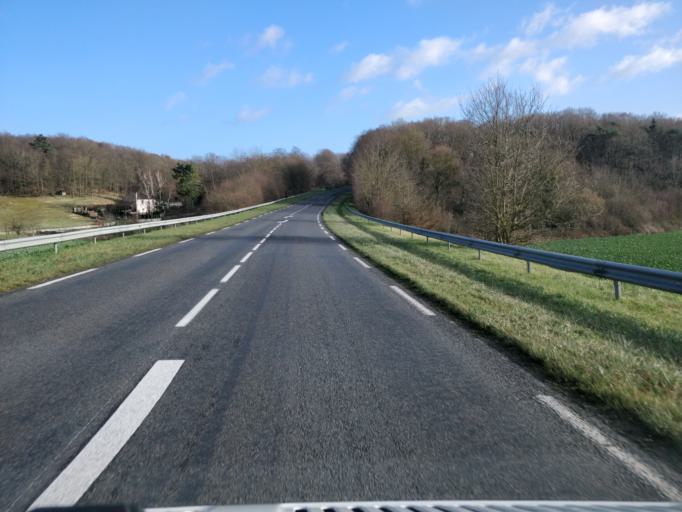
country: FR
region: Ile-de-France
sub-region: Departement de Seine-et-Marne
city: Lorrez-le-Bocage-Preaux
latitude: 48.2190
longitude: 2.9052
